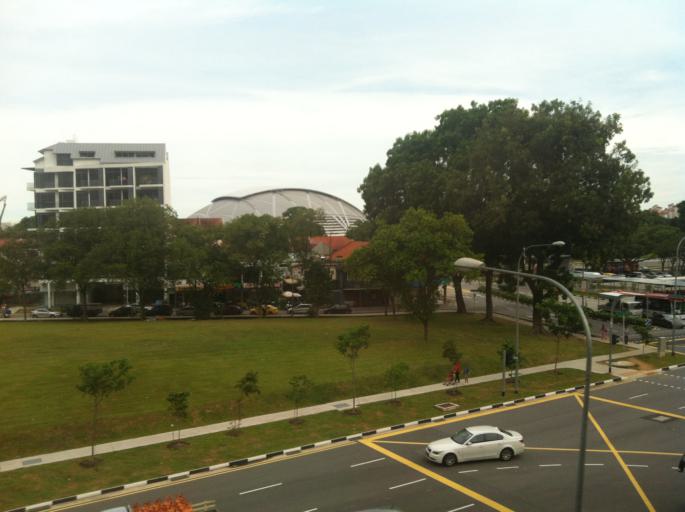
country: SG
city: Singapore
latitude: 1.3121
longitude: 103.8726
